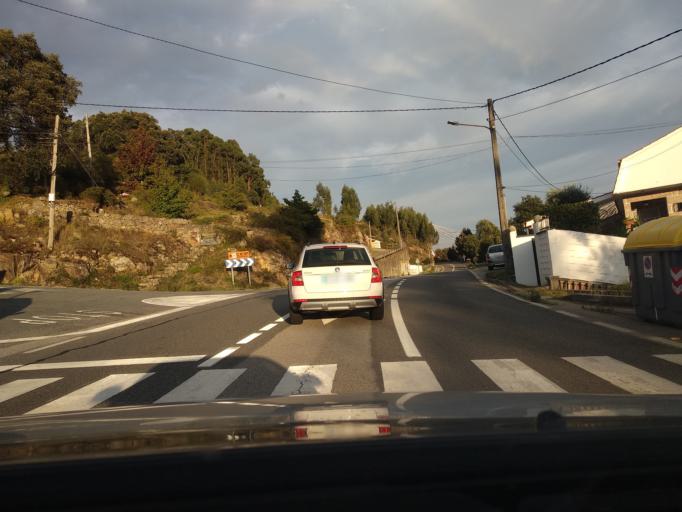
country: ES
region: Galicia
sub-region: Provincia de Pontevedra
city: Redondela
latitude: 42.2917
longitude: -8.6742
